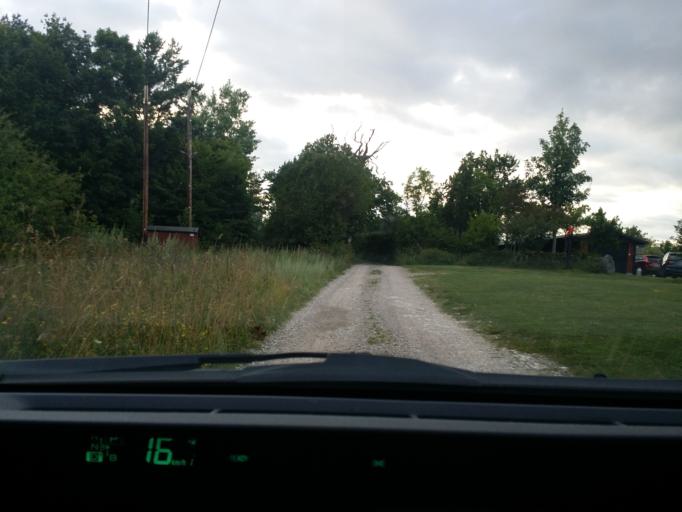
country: SE
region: Kalmar
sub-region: Borgholms Kommun
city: Borgholm
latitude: 57.2100
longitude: 16.9557
